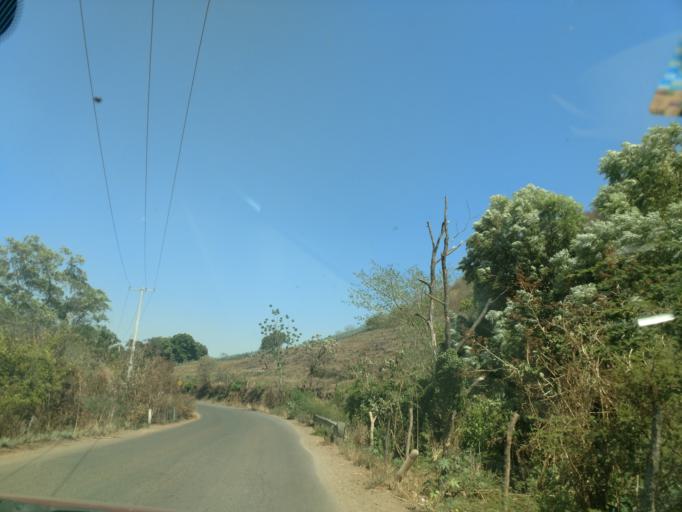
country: MX
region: Nayarit
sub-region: Tepic
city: La Corregidora
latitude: 21.4725
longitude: -104.6677
